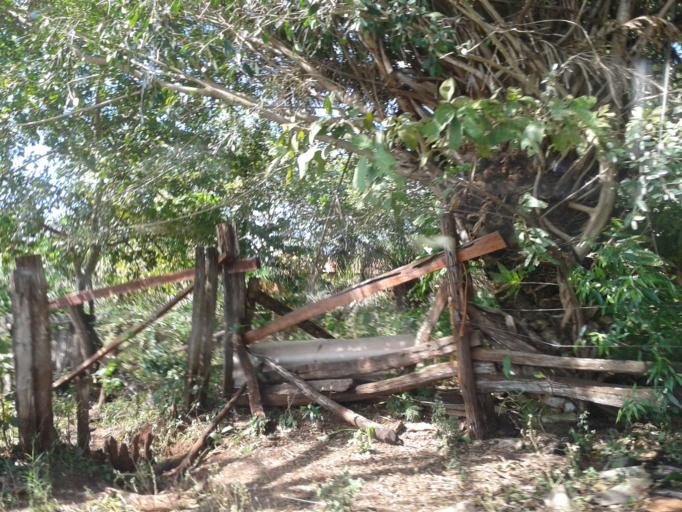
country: BR
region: Minas Gerais
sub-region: Campina Verde
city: Campina Verde
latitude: -19.4423
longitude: -49.7026
